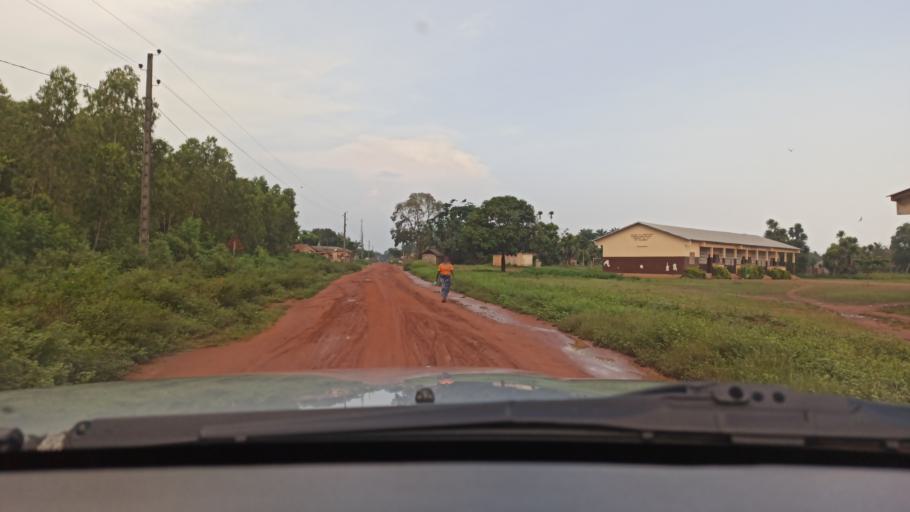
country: BJ
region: Queme
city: Porto-Novo
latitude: 6.4937
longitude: 2.6895
